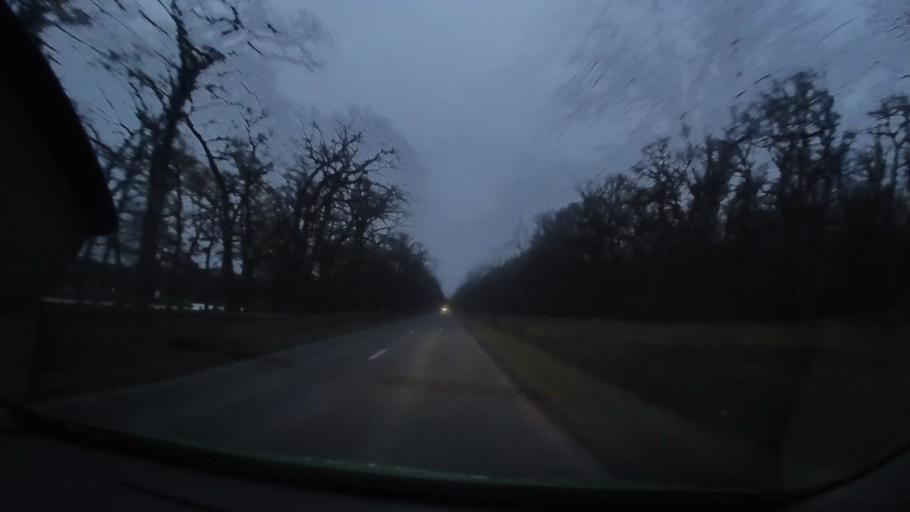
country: RO
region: Mures
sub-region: Comuna Solovastru
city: Jabenita
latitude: 46.7712
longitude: 24.7912
